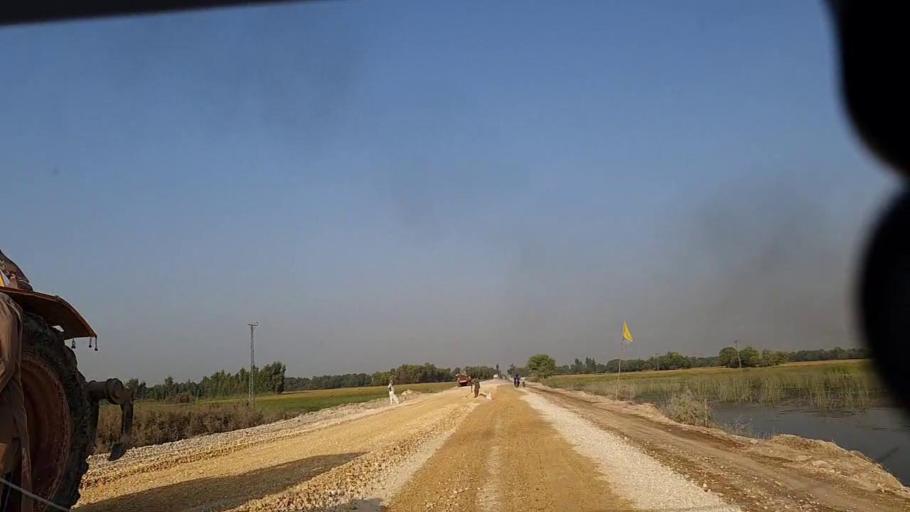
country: PK
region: Sindh
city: Chak
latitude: 27.8506
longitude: 68.8101
